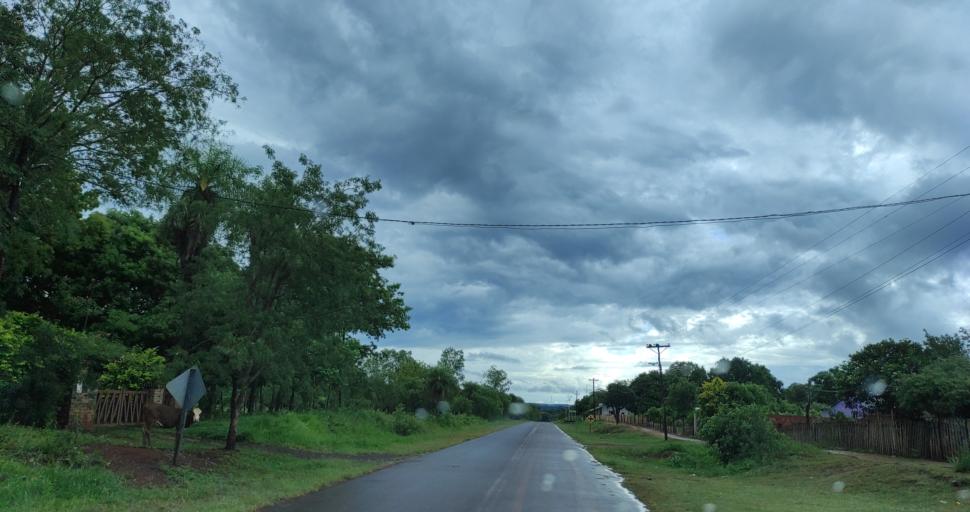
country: AR
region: Misiones
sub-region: Departamento de Apostoles
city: San Jose
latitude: -27.7723
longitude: -55.7606
